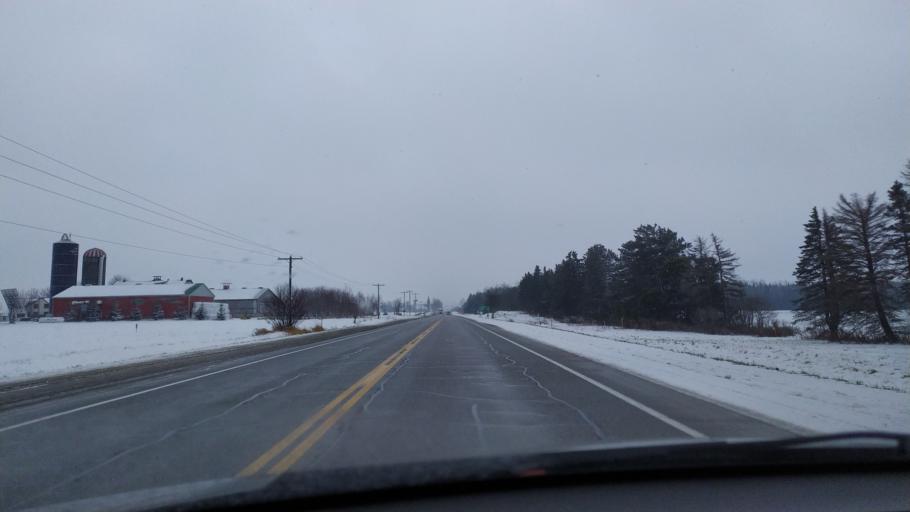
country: CA
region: Ontario
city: Waterloo
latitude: 43.6269
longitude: -80.7025
